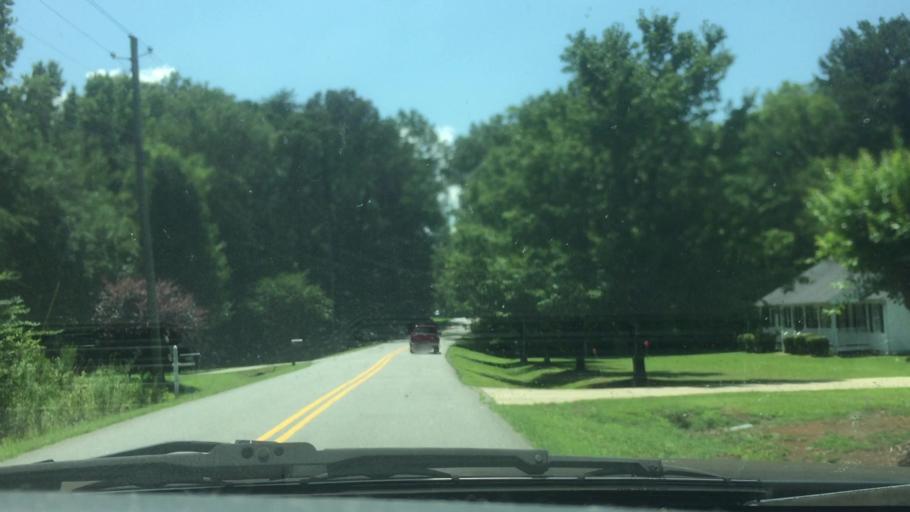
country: US
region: Georgia
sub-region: Bartow County
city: Rydal
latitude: 34.3254
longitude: -84.7052
